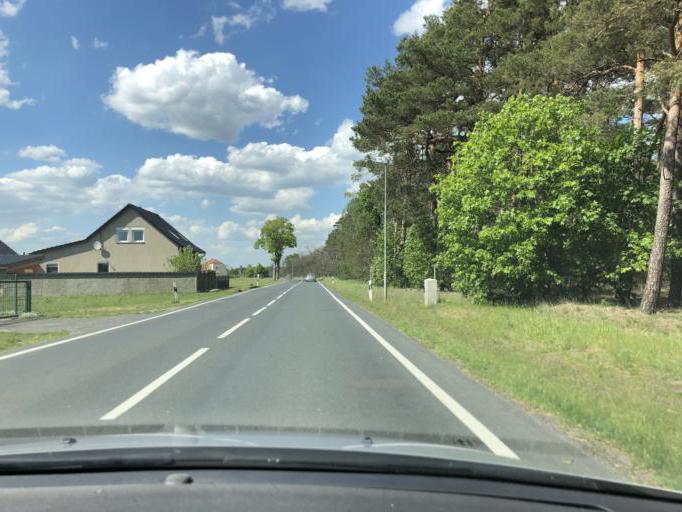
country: DE
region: Brandenburg
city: Spreenhagen
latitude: 52.3319
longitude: 13.8975
